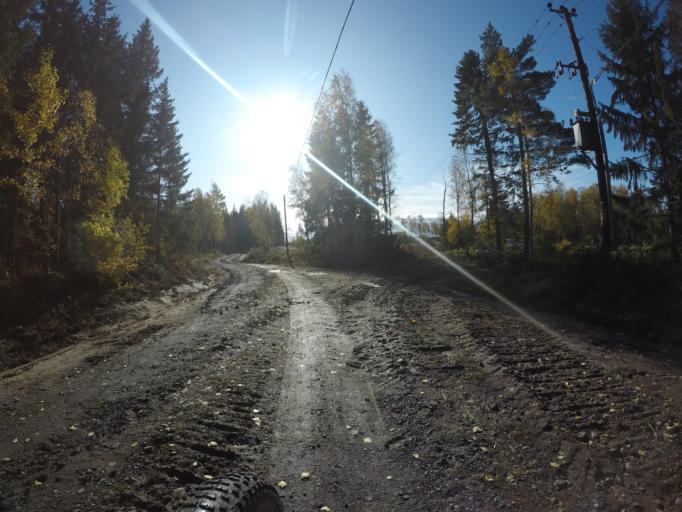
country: SE
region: Vaestmanland
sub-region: Kungsors Kommun
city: Kungsoer
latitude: 59.3118
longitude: 16.0975
